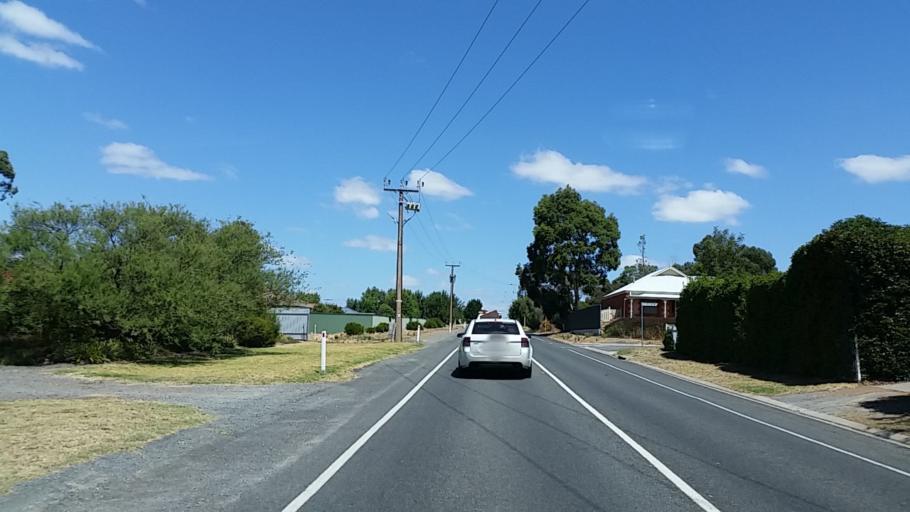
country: AU
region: South Australia
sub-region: Mount Barker
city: Nairne
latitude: -35.0251
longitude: 138.9018
